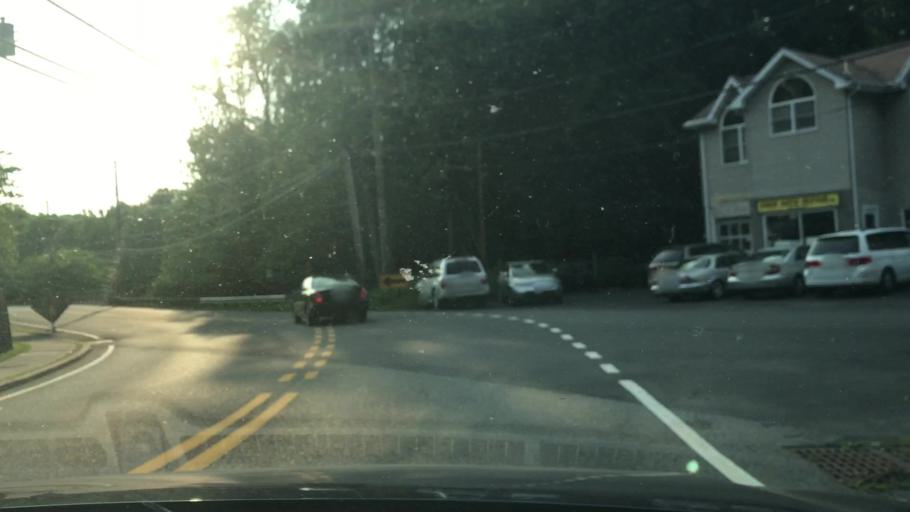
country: US
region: New Jersey
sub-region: Bergen County
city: Harrington Park
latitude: 40.9849
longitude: -73.9904
